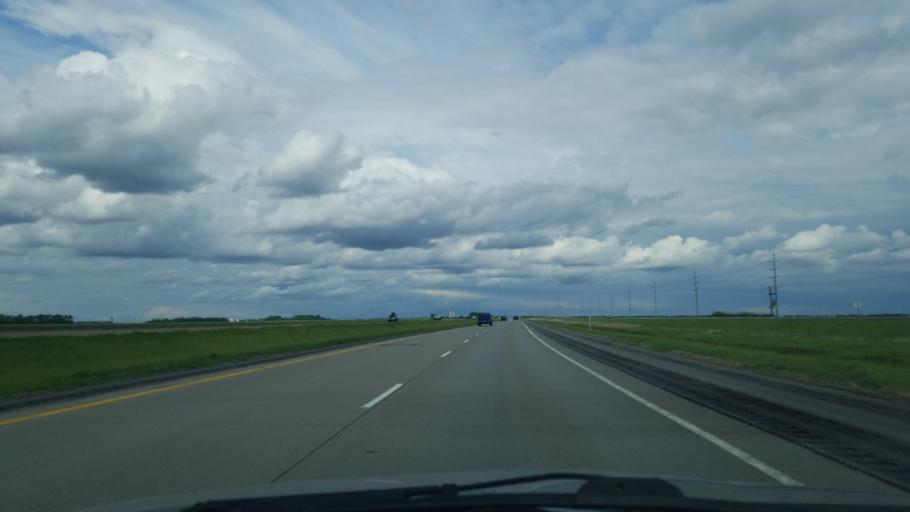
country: US
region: North Dakota
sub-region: Cass County
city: Casselton
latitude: 46.8766
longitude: -97.1910
